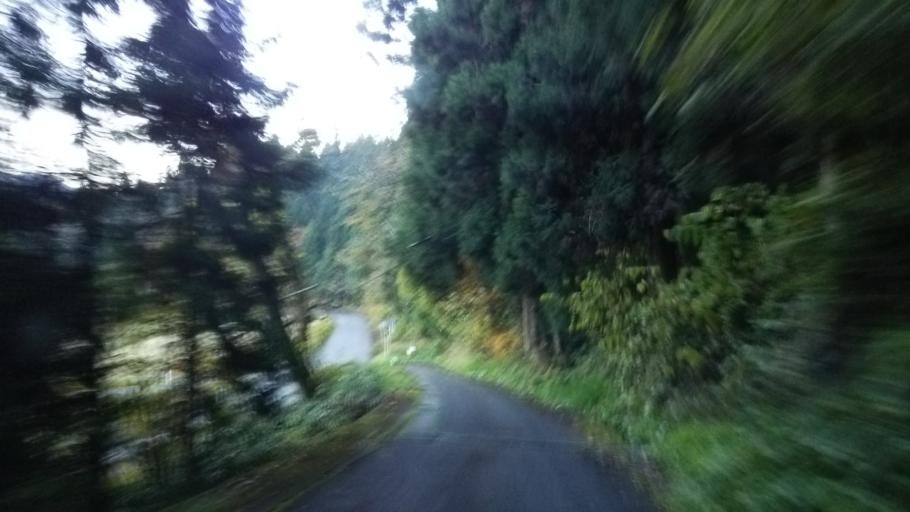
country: JP
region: Fukushima
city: Kitakata
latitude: 37.4884
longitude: 139.6632
